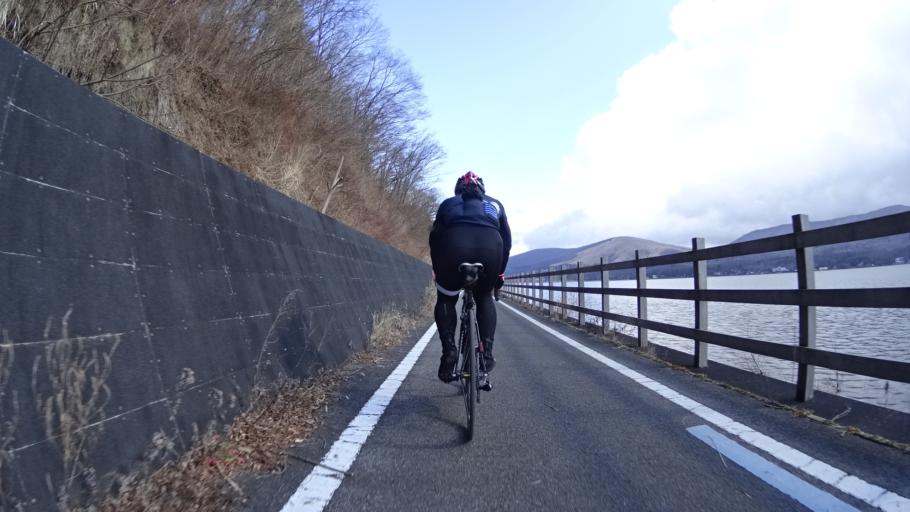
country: JP
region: Shizuoka
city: Gotemba
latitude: 35.4212
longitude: 138.8855
